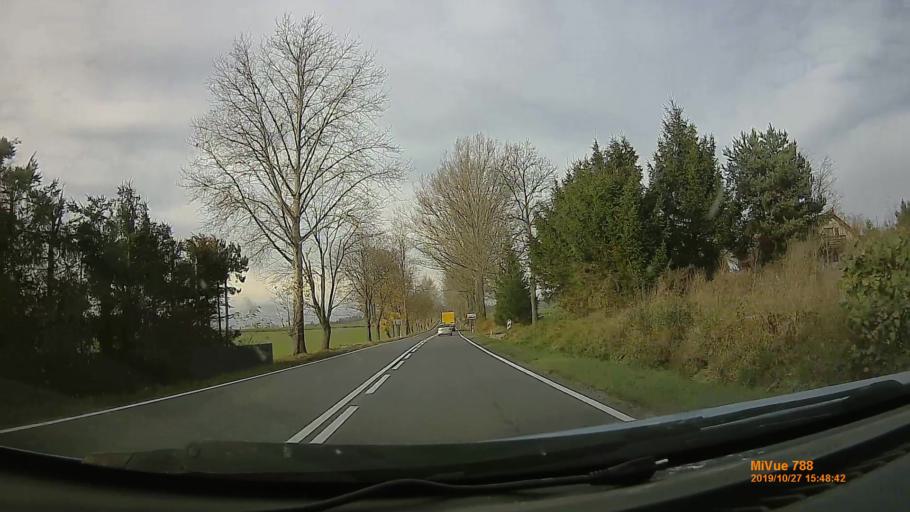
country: PL
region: Lower Silesian Voivodeship
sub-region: Powiat klodzki
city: Bozkow
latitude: 50.4995
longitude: 16.5851
